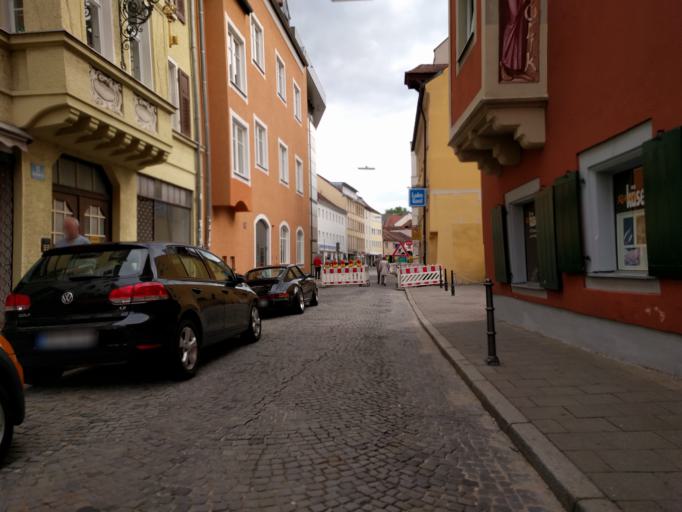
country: DE
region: Bavaria
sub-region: Upper Palatinate
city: Regensburg
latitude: 49.0172
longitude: 12.0997
